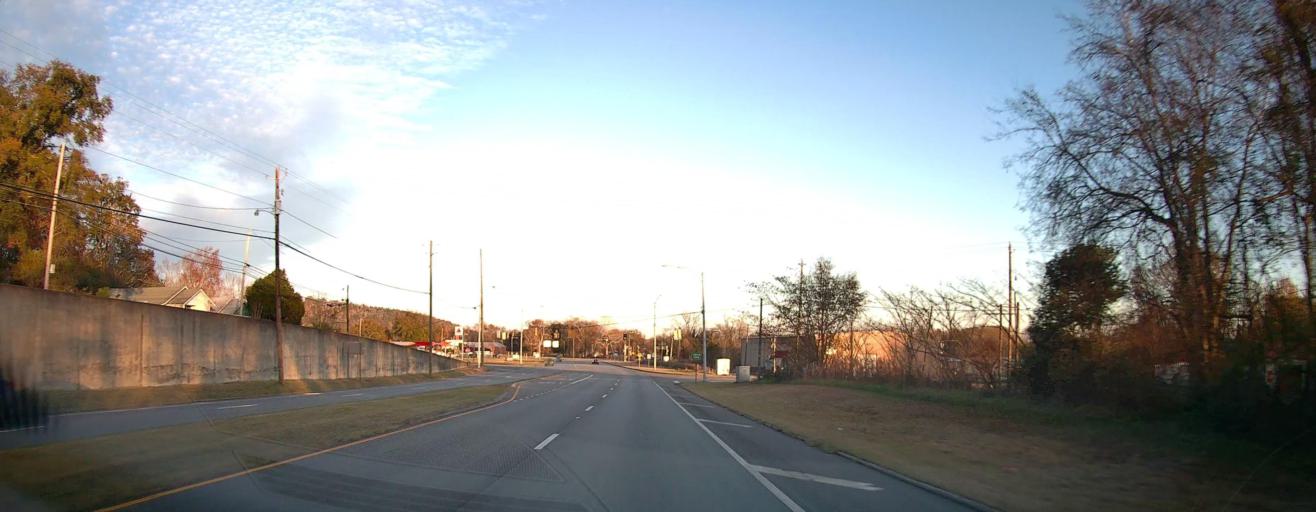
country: US
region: Alabama
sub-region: Etowah County
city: Attalla
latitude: 34.0184
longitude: -86.0970
